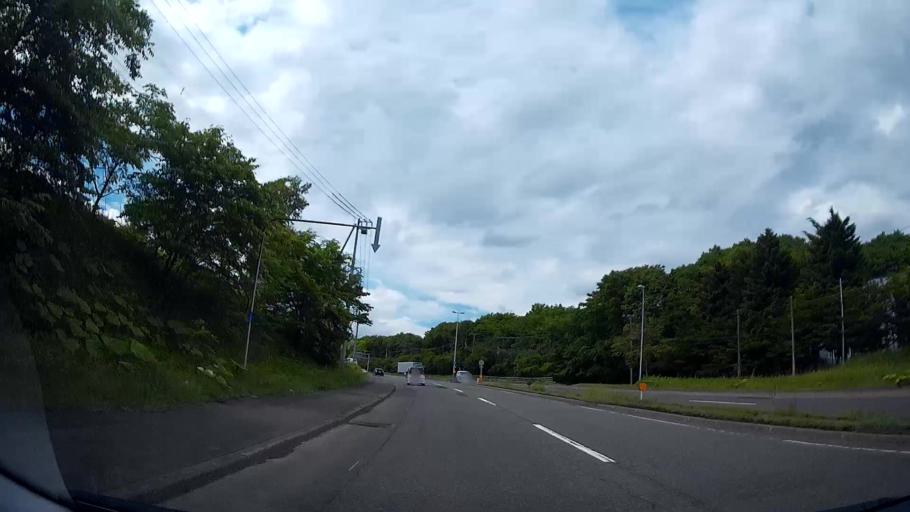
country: JP
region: Hokkaido
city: Chitose
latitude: 42.8555
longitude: 141.6090
